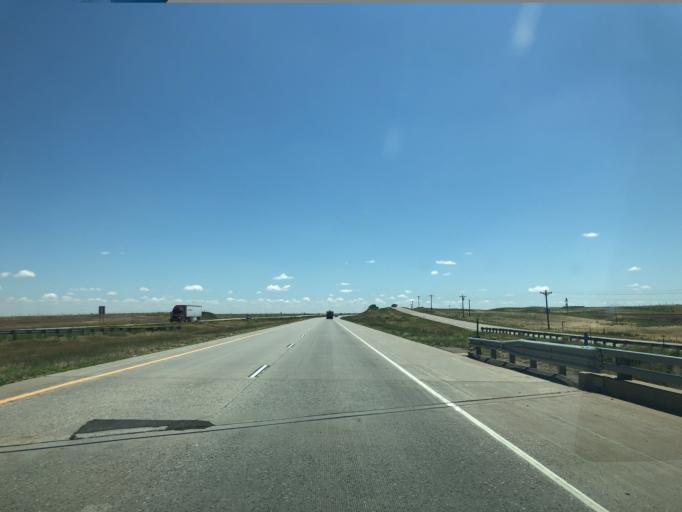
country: US
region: Colorado
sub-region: Arapahoe County
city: Byers
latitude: 39.6882
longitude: -104.1293
